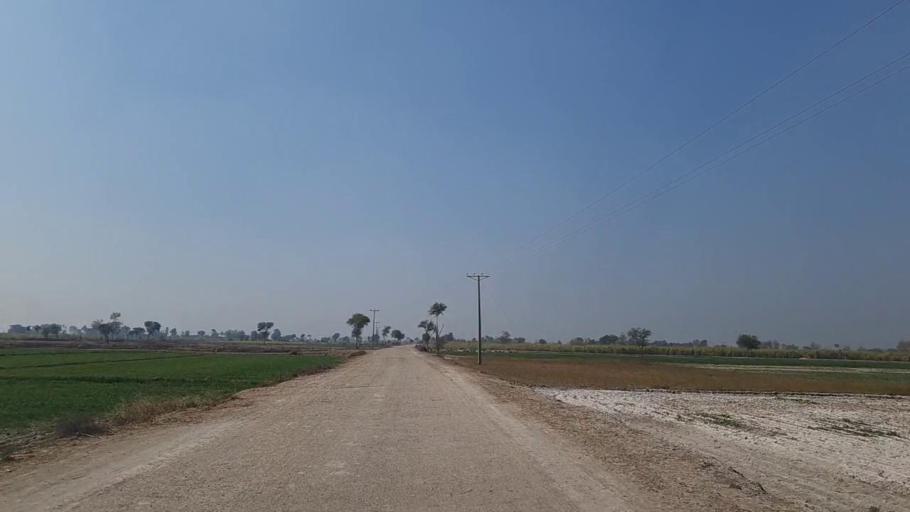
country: PK
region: Sindh
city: Daur
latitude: 26.5032
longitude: 68.3192
